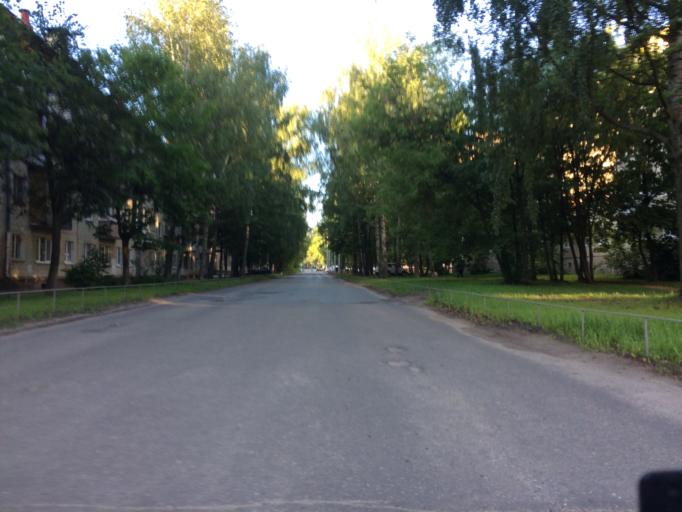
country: RU
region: Mariy-El
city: Yoshkar-Ola
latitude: 56.6412
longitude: 47.8785
